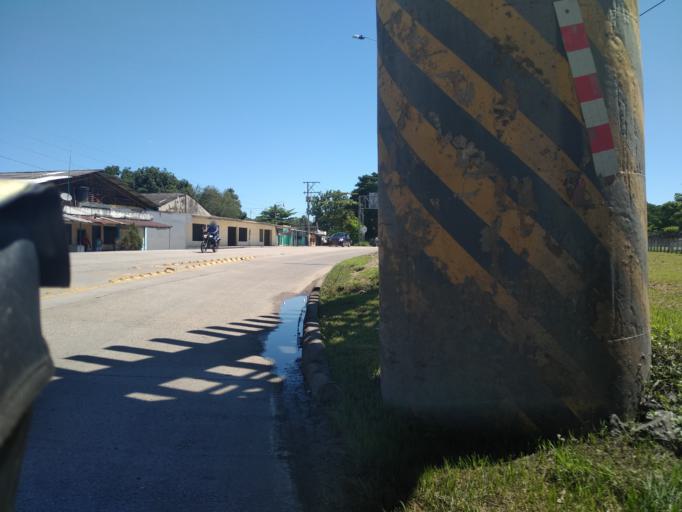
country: CO
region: Cundinamarca
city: Puerto Salgar
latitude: 5.4682
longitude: -74.6604
